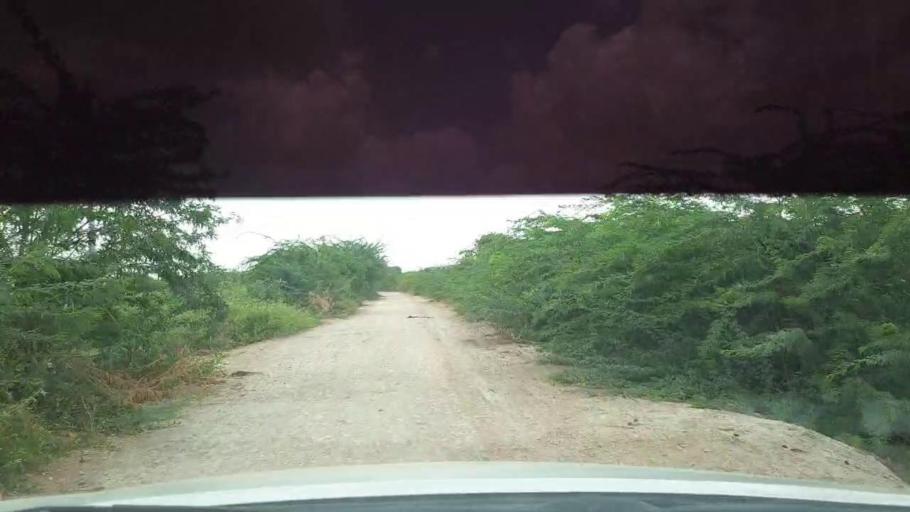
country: PK
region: Sindh
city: Kadhan
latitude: 24.4643
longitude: 69.0460
